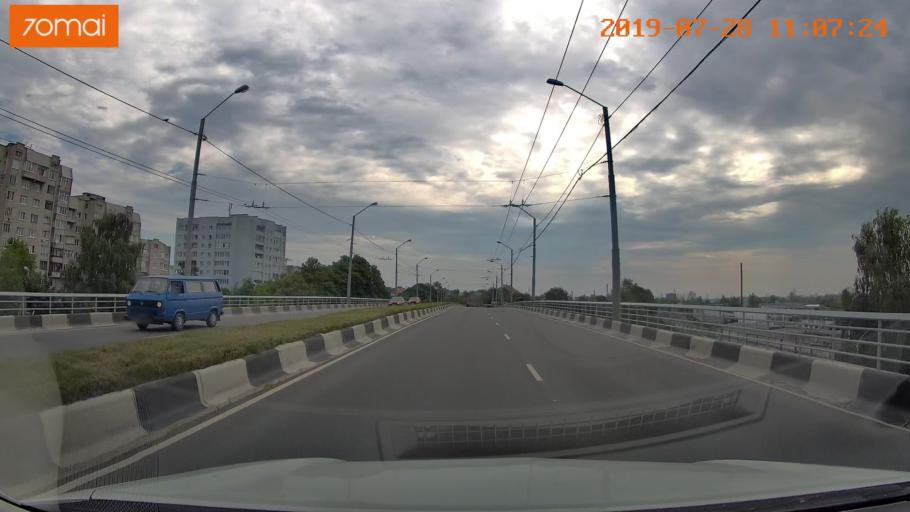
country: RU
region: Kaliningrad
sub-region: Gorod Kaliningrad
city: Kaliningrad
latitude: 54.7119
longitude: 20.4281
